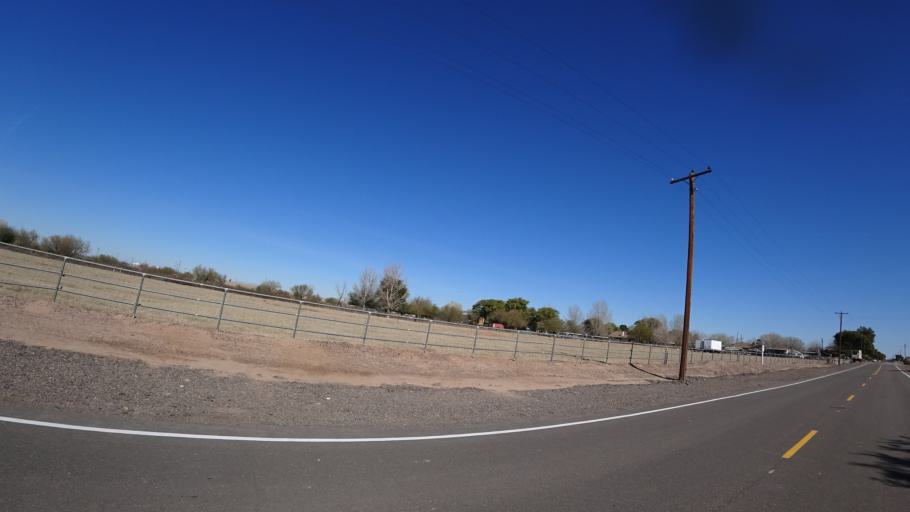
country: US
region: Arizona
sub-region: Maricopa County
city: Avondale
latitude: 33.3918
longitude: -112.3428
